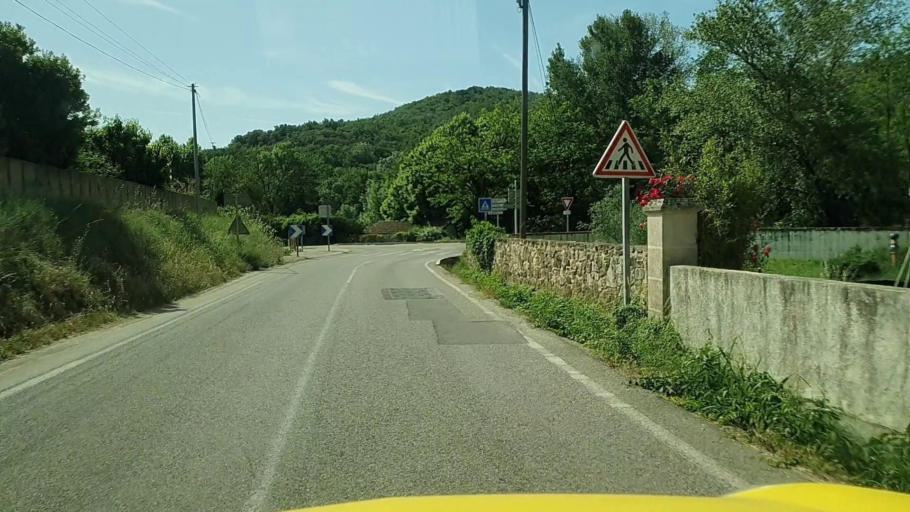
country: FR
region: Languedoc-Roussillon
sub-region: Departement du Gard
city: Tresques
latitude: 44.0956
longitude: 4.5544
